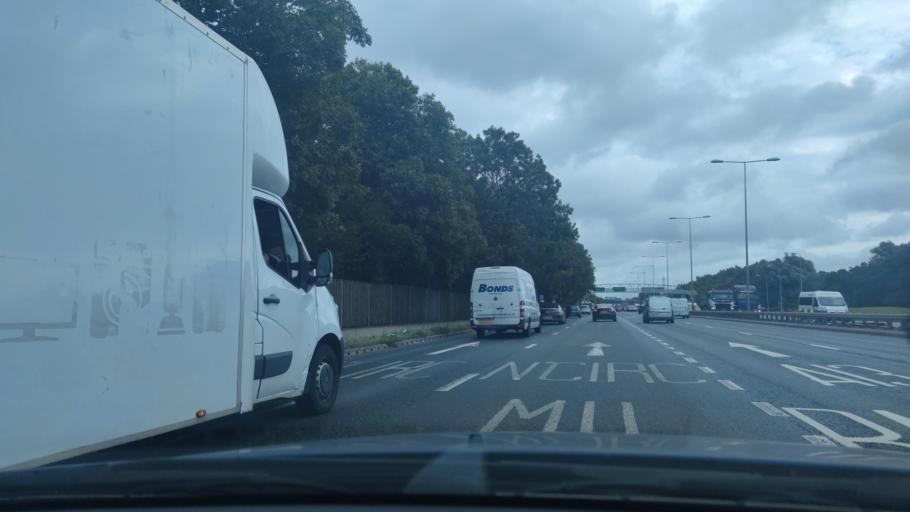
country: GB
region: England
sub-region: Greater London
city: East Ham
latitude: 51.5230
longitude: 0.0655
